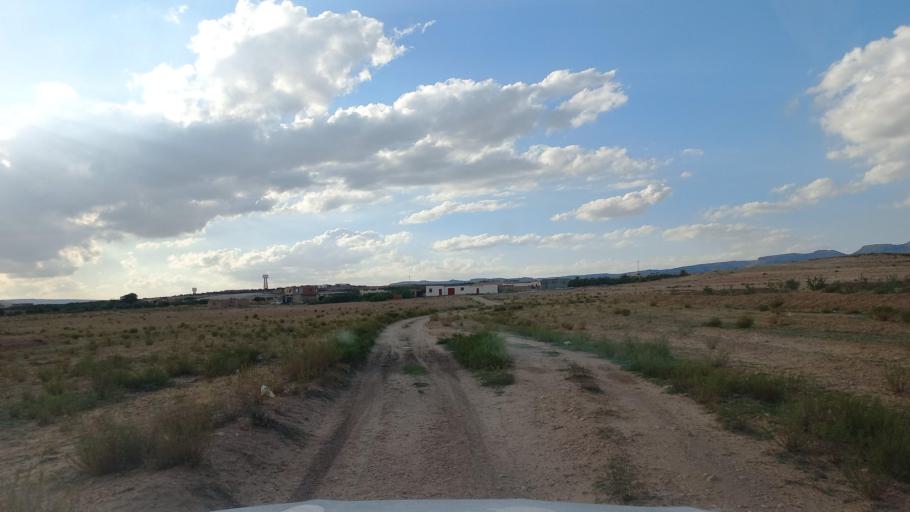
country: TN
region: Al Qasrayn
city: Sbiba
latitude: 35.3885
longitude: 9.0544
